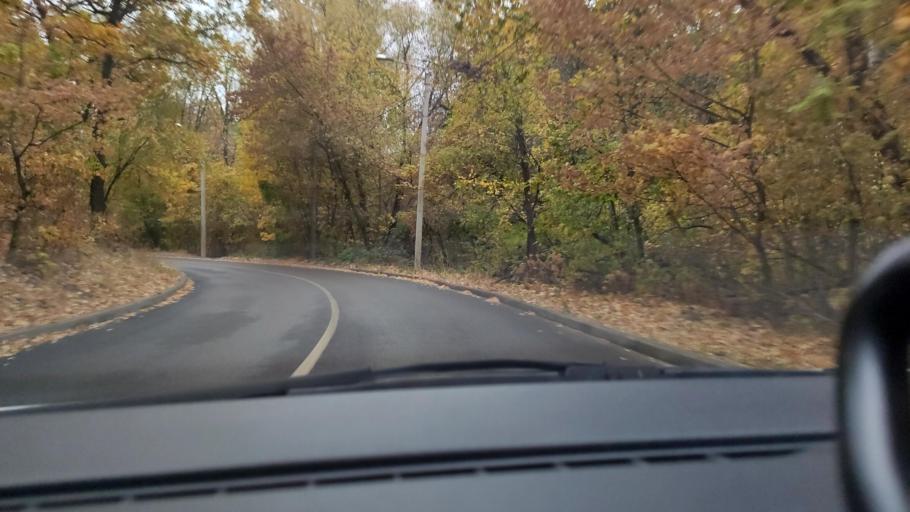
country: RU
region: Voronezj
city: Voronezh
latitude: 51.7191
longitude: 39.2350
